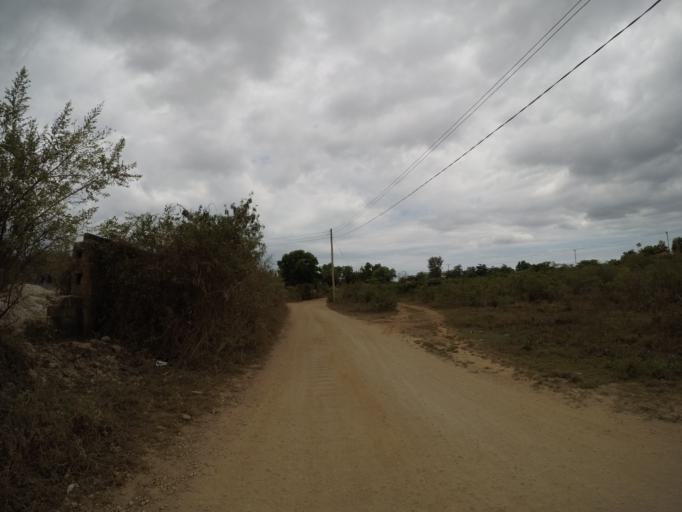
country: TZ
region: Zanzibar Central/South
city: Koani
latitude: -6.1965
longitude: 39.3095
